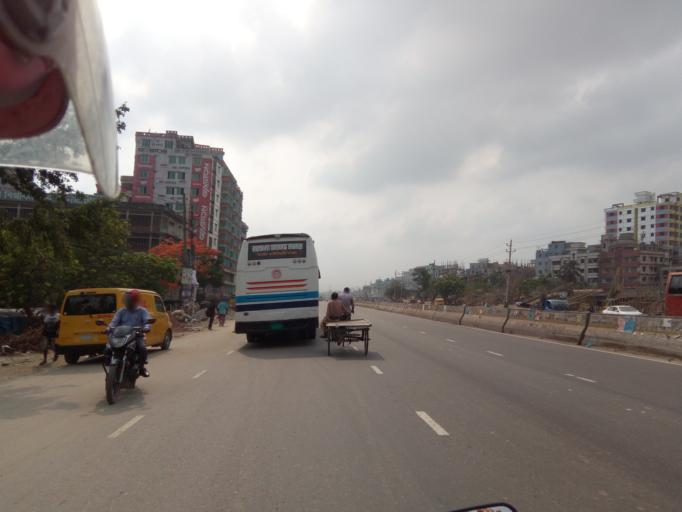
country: BD
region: Dhaka
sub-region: Dhaka
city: Dhaka
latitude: 23.7038
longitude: 90.4482
